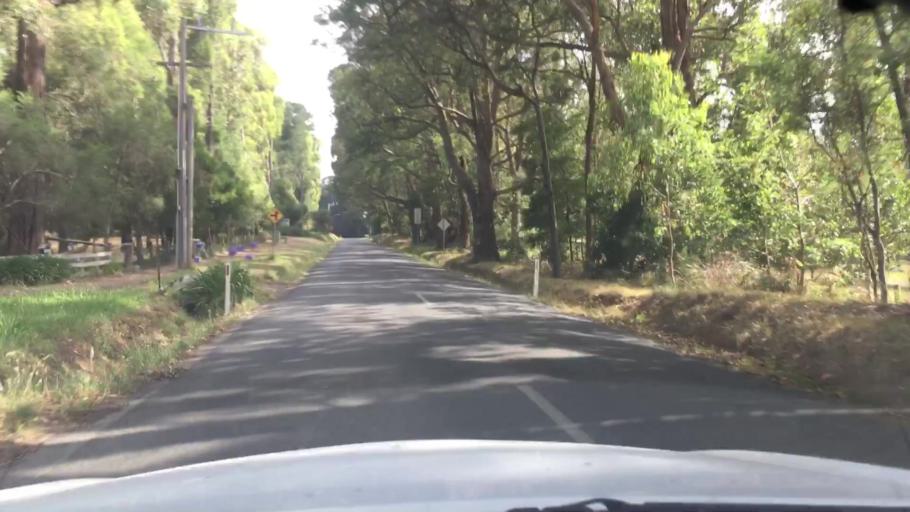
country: AU
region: Victoria
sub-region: Yarra Ranges
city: Macclesfield
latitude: -37.8882
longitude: 145.4761
